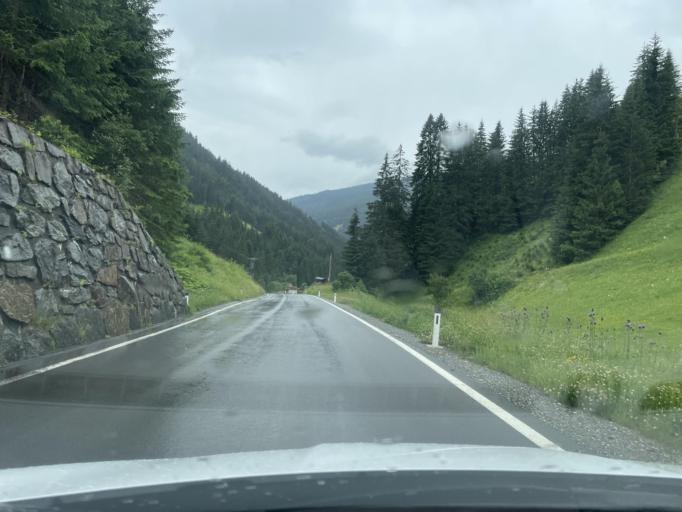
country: AT
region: Tyrol
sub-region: Politischer Bezirk Lienz
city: Ausservillgraten
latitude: 46.7943
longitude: 12.4444
